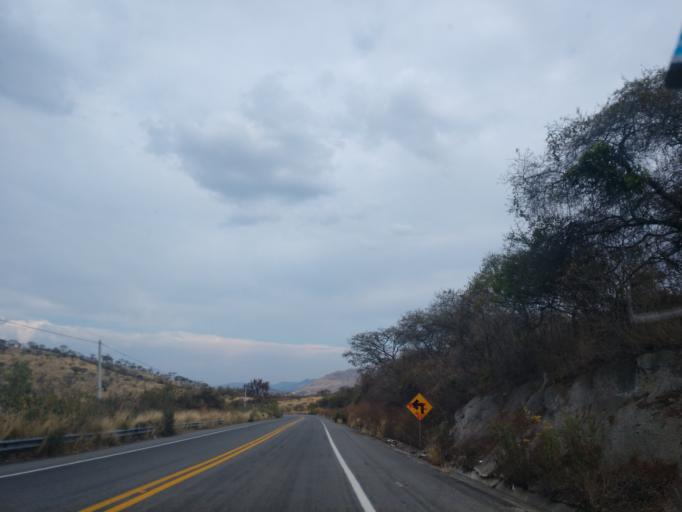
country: MX
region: Jalisco
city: La Manzanilla de la Paz
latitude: 20.1056
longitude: -103.1649
